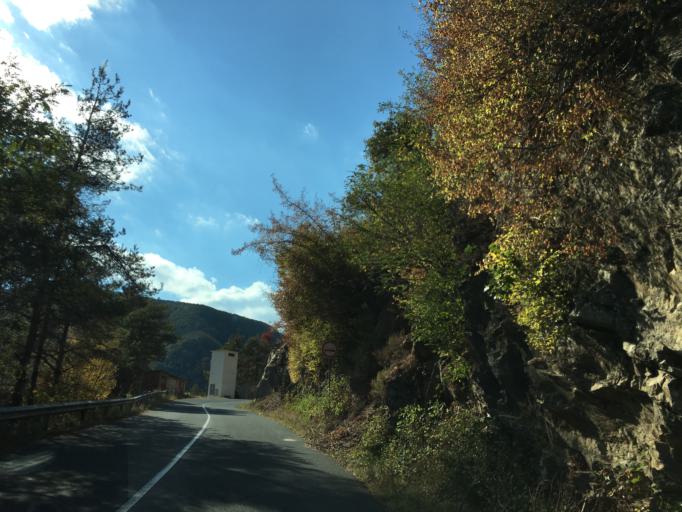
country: BG
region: Smolyan
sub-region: Obshtina Nedelino
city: Nedelino
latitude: 41.4385
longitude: 25.0117
